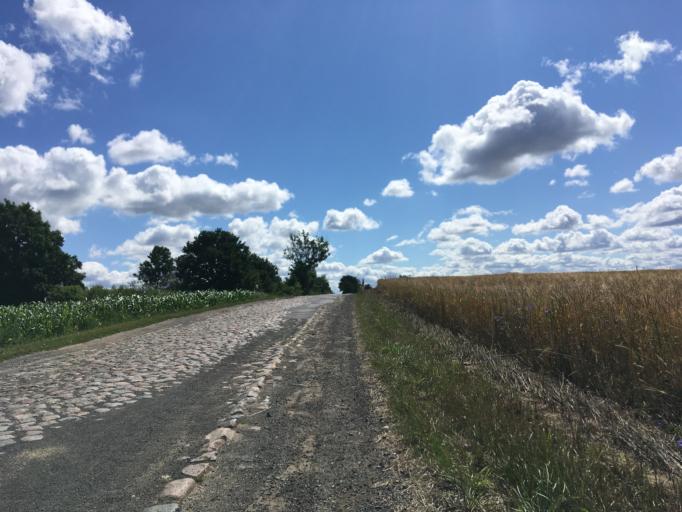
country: DE
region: Brandenburg
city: Mittenwalde
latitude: 53.1917
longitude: 13.6328
